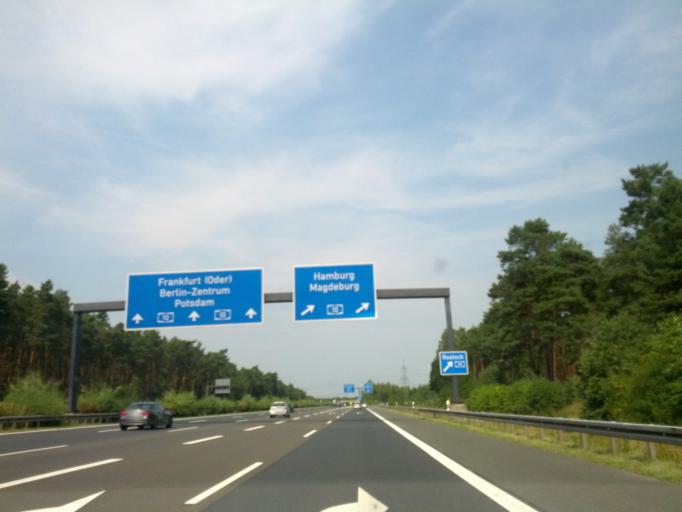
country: DE
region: Brandenburg
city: Fichtenwalde
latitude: 52.2797
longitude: 12.9130
